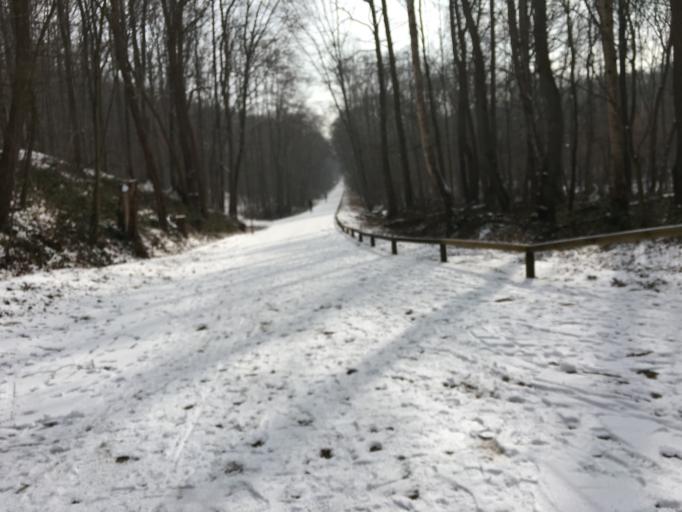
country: DE
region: North Rhine-Westphalia
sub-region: Regierungsbezirk Koln
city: Kreuzau
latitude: 50.7739
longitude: 6.5009
